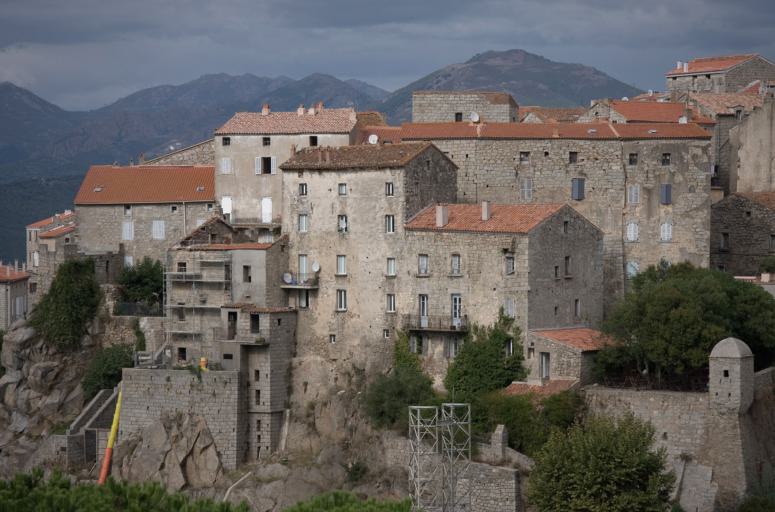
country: FR
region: Corsica
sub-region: Departement de la Corse-du-Sud
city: Sartene
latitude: 41.6192
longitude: 8.9704
